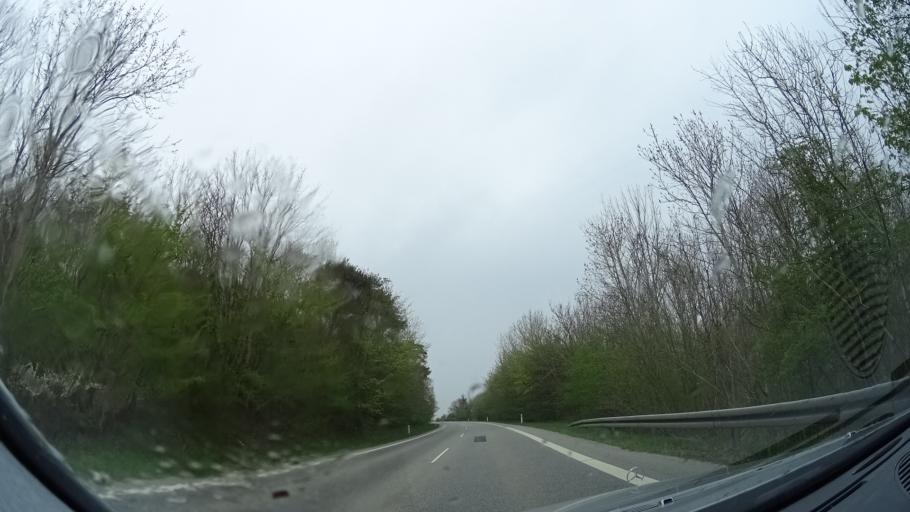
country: DK
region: Zealand
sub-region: Lejre Kommune
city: Ejby
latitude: 55.6891
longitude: 11.7932
